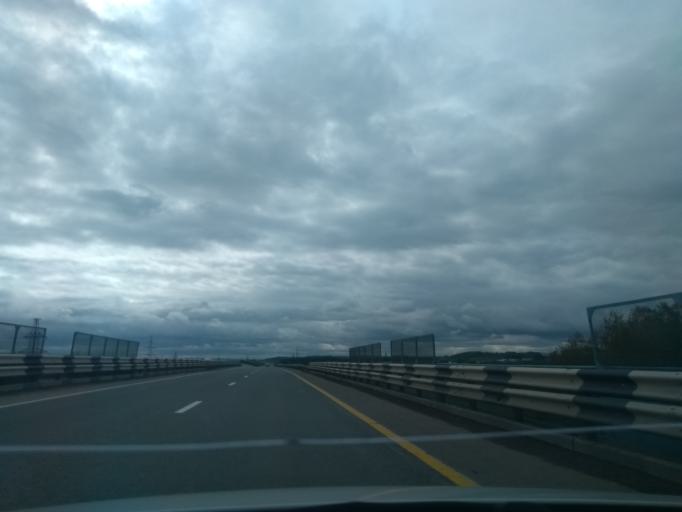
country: RU
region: Perm
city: Froly
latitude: 57.9311
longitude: 56.2968
